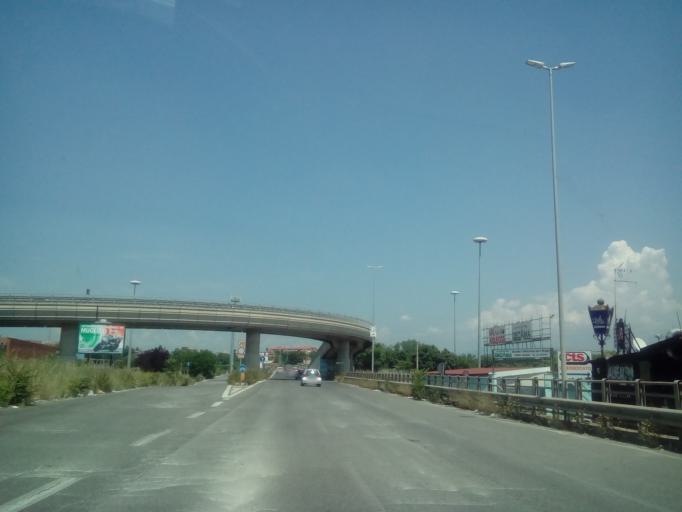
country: IT
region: Latium
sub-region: Citta metropolitana di Roma Capitale
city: Rome
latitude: 41.9185
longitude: 12.5645
